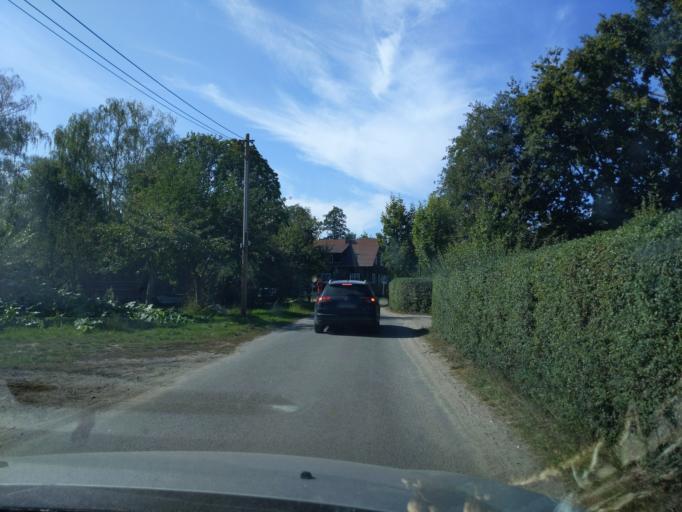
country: DE
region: Brandenburg
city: Straupitz
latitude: 51.8635
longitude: 14.0857
